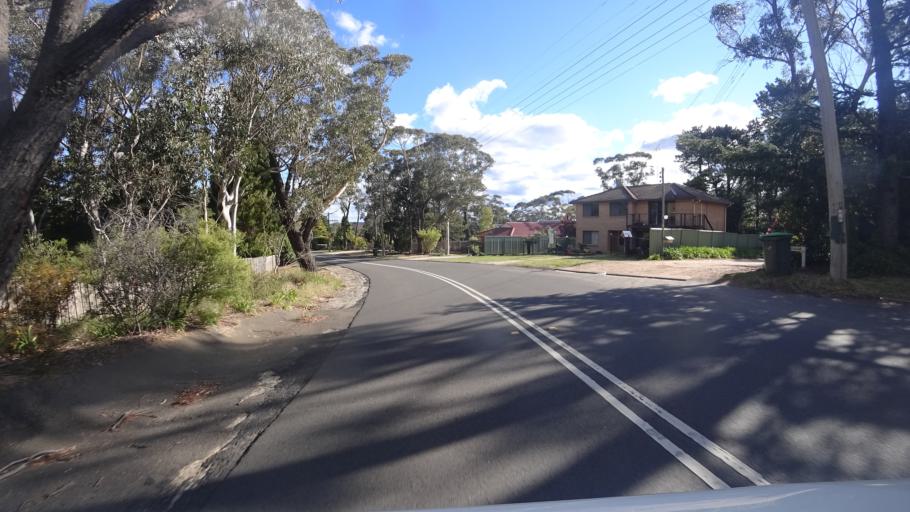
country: AU
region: New South Wales
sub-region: Blue Mountains Municipality
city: Katoomba
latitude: -33.7189
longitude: 150.2940
